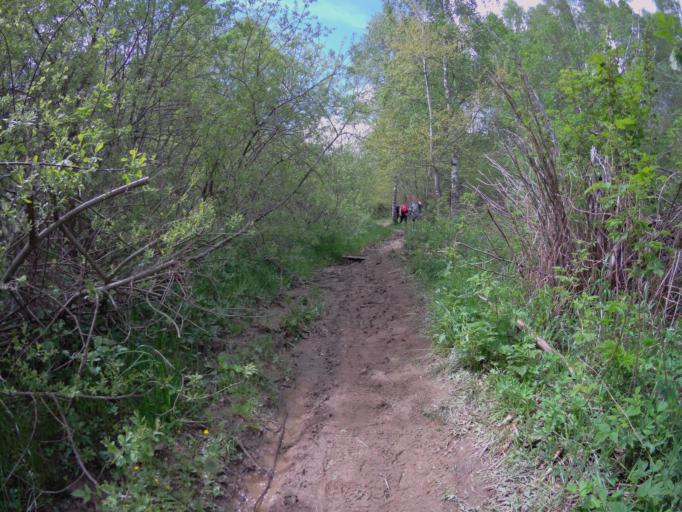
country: PL
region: Subcarpathian Voivodeship
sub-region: Powiat bieszczadzki
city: Lutowiska
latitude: 49.1436
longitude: 22.5657
